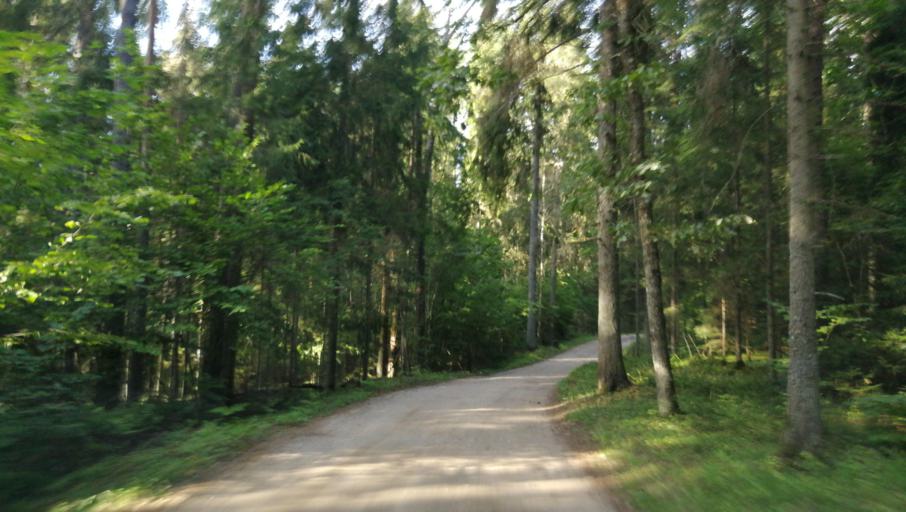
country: LV
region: Cesu Rajons
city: Cesis
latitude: 57.2879
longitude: 25.2113
